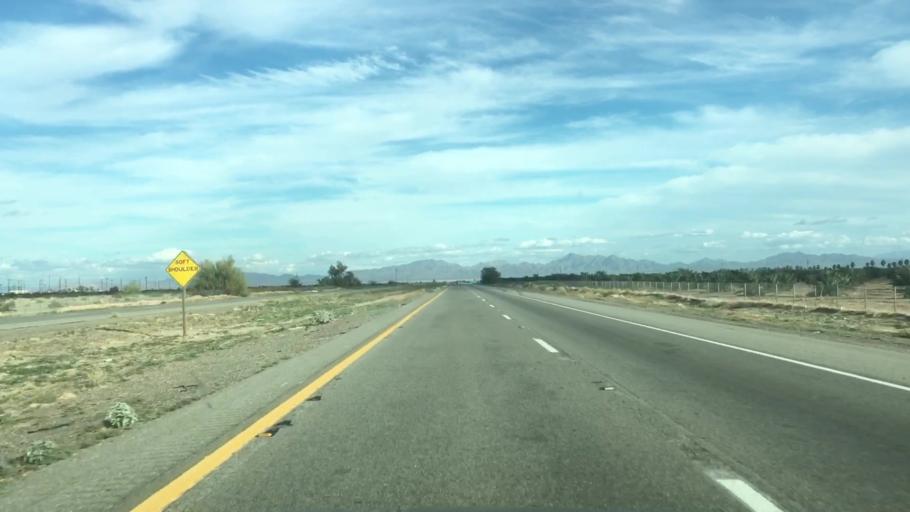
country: US
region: California
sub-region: Riverside County
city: Mesa Verde
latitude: 33.6066
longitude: -114.6904
